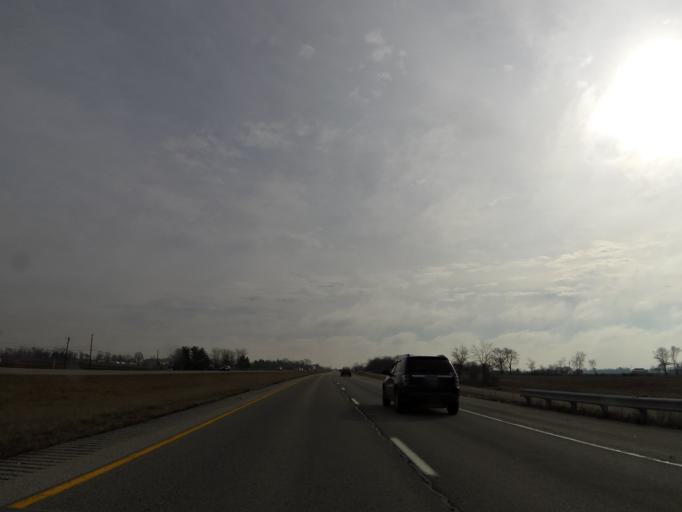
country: US
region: Indiana
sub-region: Hancock County
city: New Palestine
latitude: 39.6310
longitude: -85.8900
